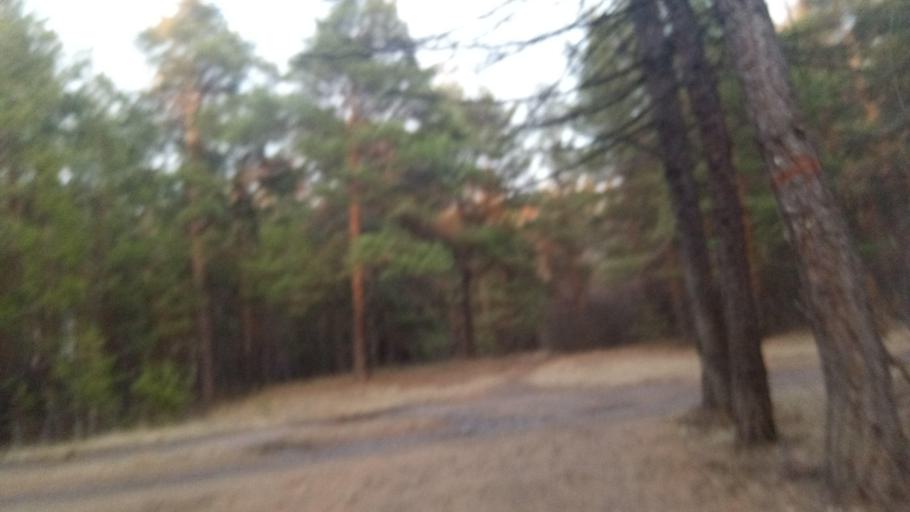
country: RU
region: Chelyabinsk
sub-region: Gorod Chelyabinsk
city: Chelyabinsk
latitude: 55.1567
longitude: 61.3333
